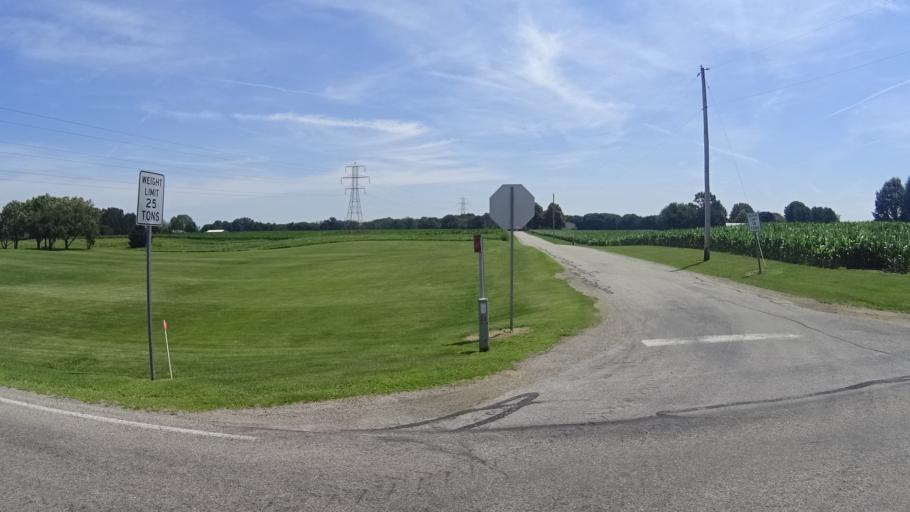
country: US
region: Ohio
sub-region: Erie County
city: Huron
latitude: 41.3579
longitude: -82.5176
